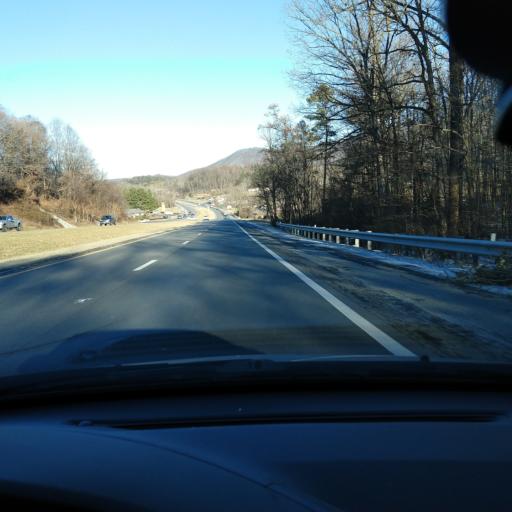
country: US
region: Virginia
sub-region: Botetourt County
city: Blue Ridge
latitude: 37.3628
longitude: -79.8232
